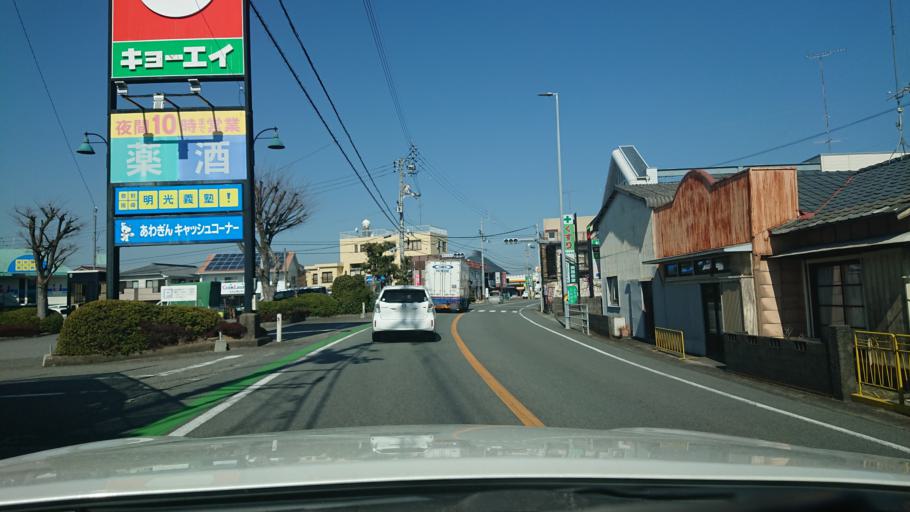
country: JP
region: Tokushima
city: Komatsushimacho
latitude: 33.9632
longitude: 134.6206
